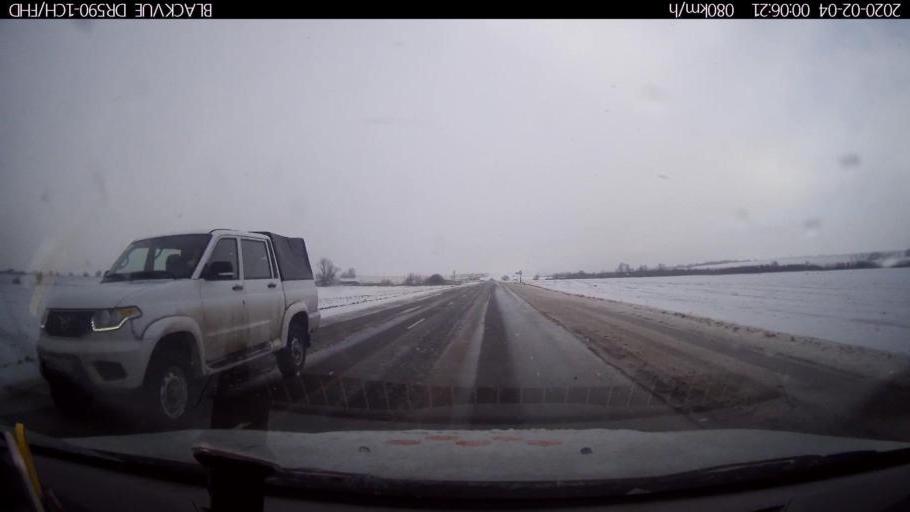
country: RU
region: Nizjnij Novgorod
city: Dal'neye Konstantinovo
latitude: 55.8472
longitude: 44.1280
